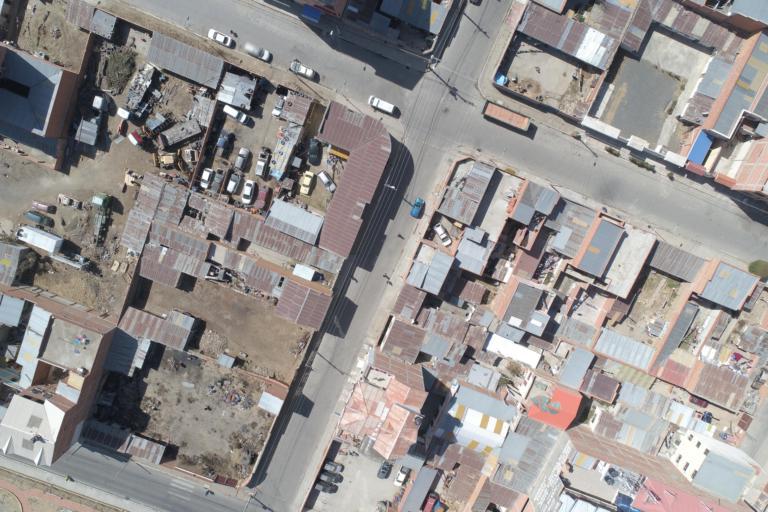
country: BO
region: La Paz
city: La Paz
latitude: -16.5264
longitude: -68.1587
